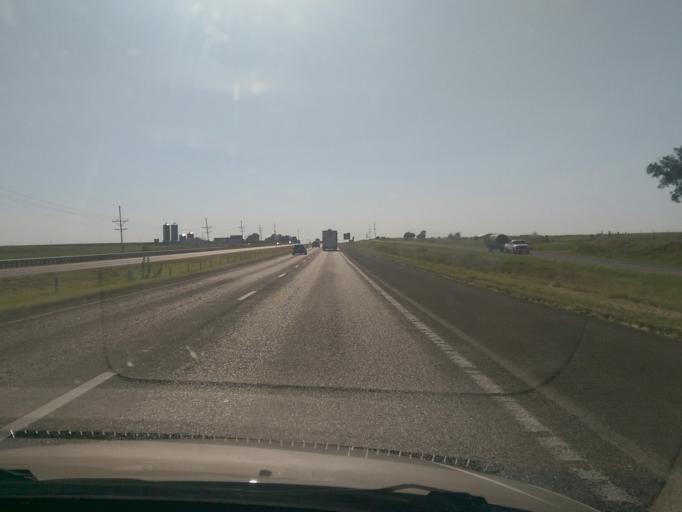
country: US
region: Missouri
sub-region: Lafayette County
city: Concordia
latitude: 38.9888
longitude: -93.5406
